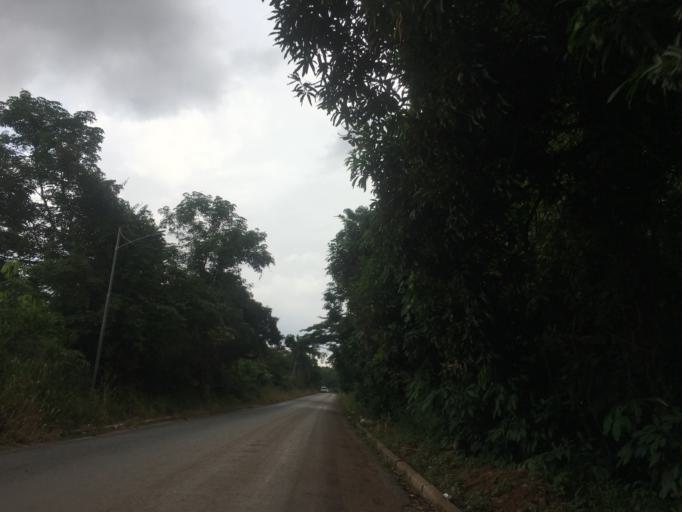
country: GH
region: Ashanti
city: Mamponteng
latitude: 6.6841
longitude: -1.5614
